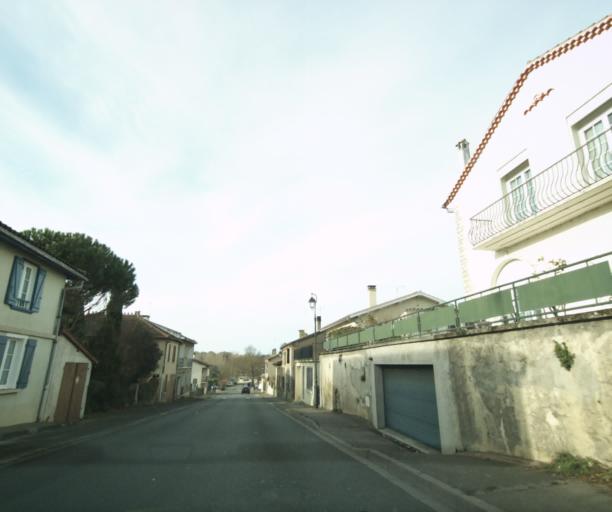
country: FR
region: Midi-Pyrenees
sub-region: Departement du Gers
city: Gimont
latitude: 43.6288
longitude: 0.8750
